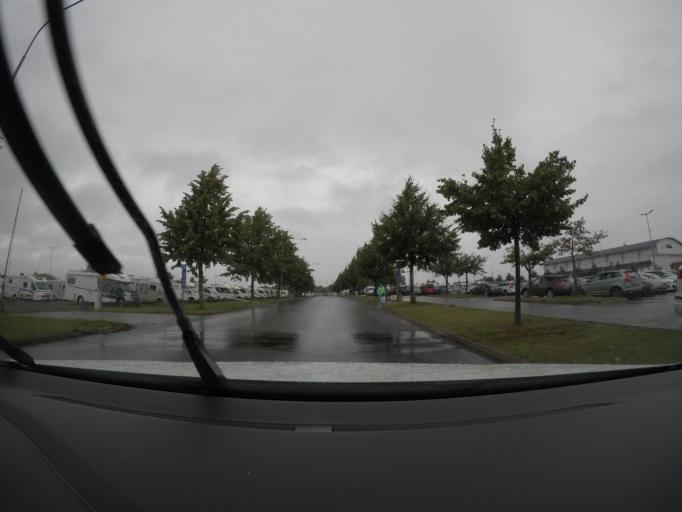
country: SE
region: Joenkoeping
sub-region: Jonkopings Kommun
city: Jonkoping
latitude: 57.7875
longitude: 14.2260
